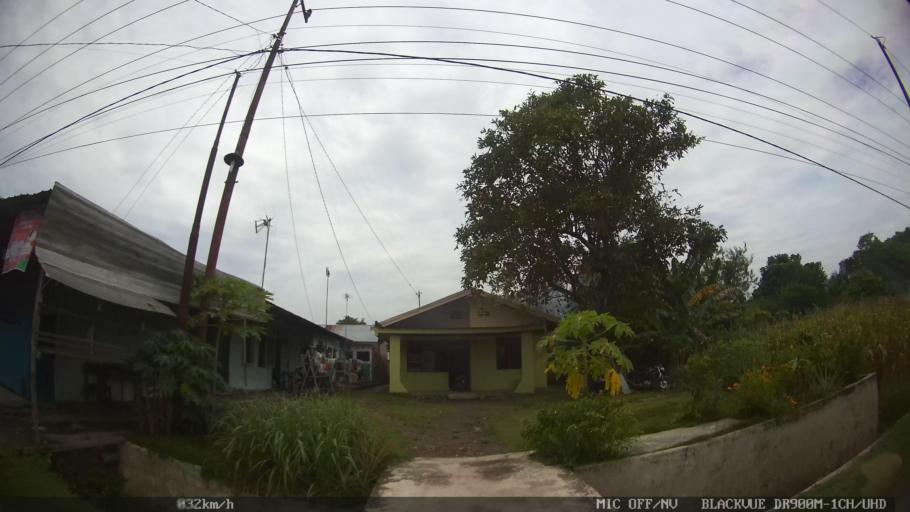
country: ID
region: North Sumatra
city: Sunggal
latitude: 3.6300
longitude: 98.5594
